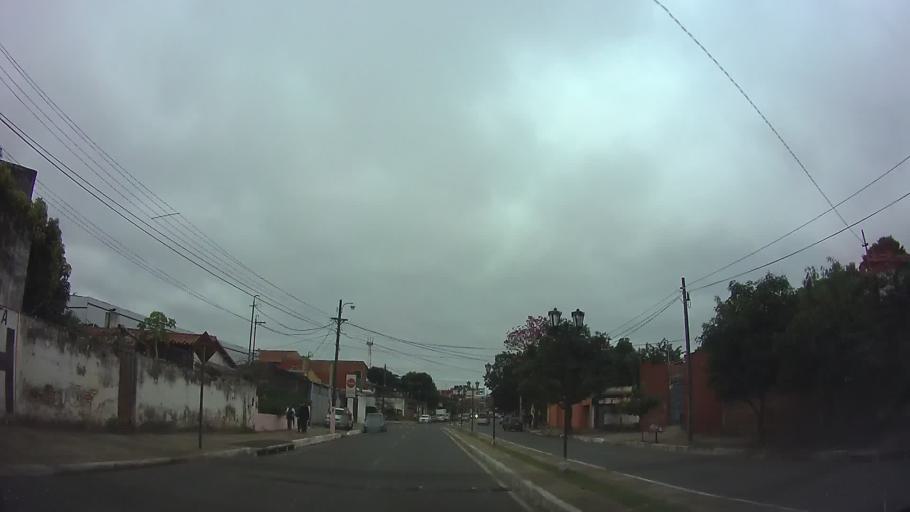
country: PY
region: Asuncion
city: Asuncion
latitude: -25.3070
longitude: -57.6258
